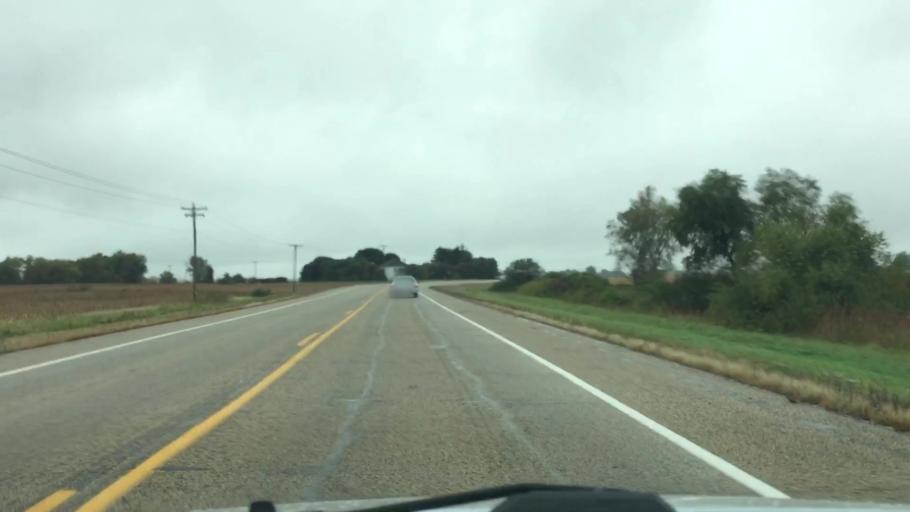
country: US
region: Wisconsin
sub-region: Jefferson County
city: Palmyra
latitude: 42.8643
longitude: -88.6491
